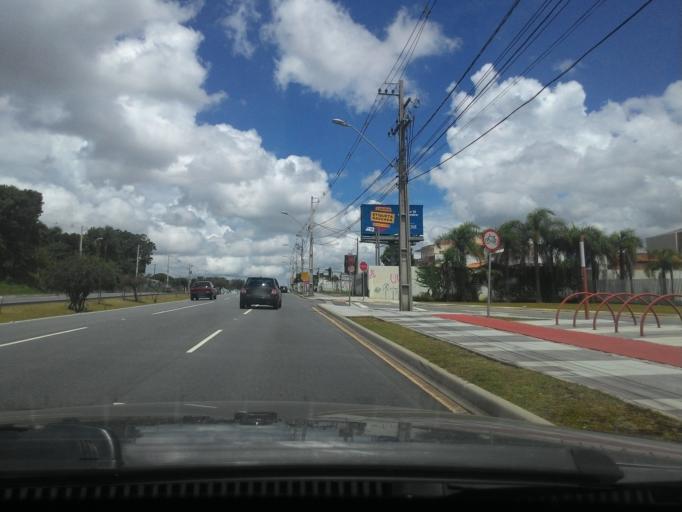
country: BR
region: Parana
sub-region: Sao Jose Dos Pinhais
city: Sao Jose dos Pinhais
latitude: -25.4898
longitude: -49.2254
